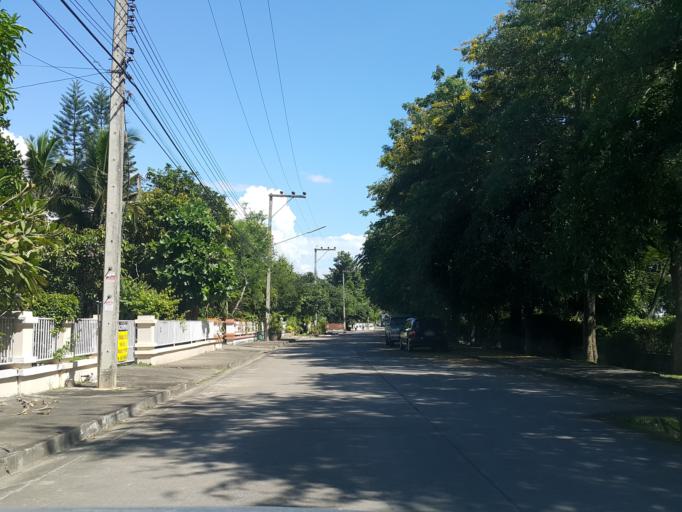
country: TH
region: Chiang Mai
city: San Sai
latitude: 18.8488
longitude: 99.0088
